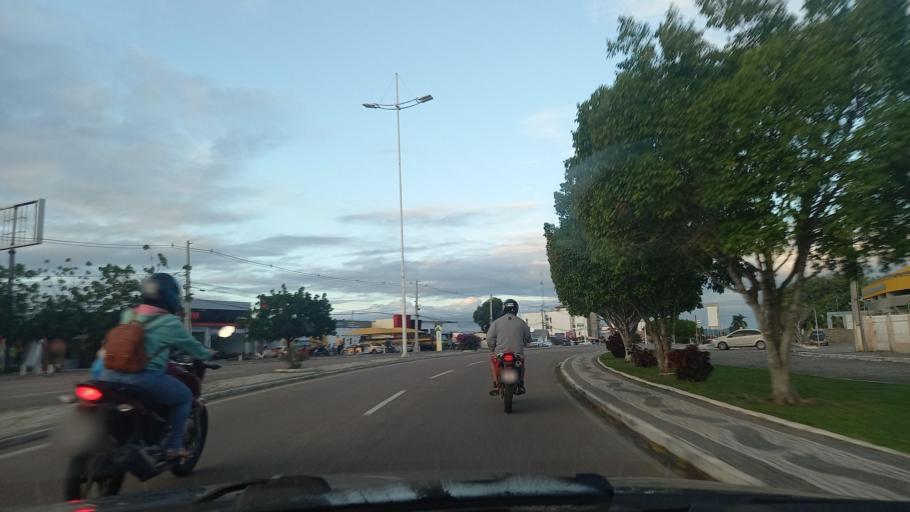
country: BR
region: Bahia
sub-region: Paulo Afonso
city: Paulo Afonso
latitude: -9.3987
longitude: -38.2311
